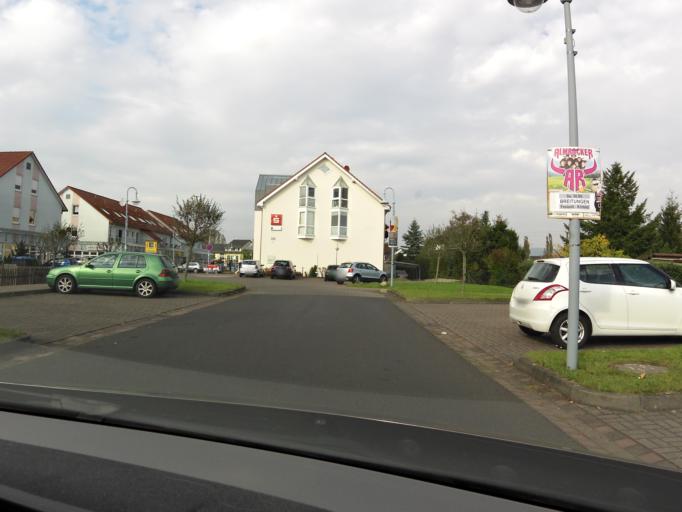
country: DE
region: Thuringia
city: Breitungen
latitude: 50.7576
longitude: 10.3307
